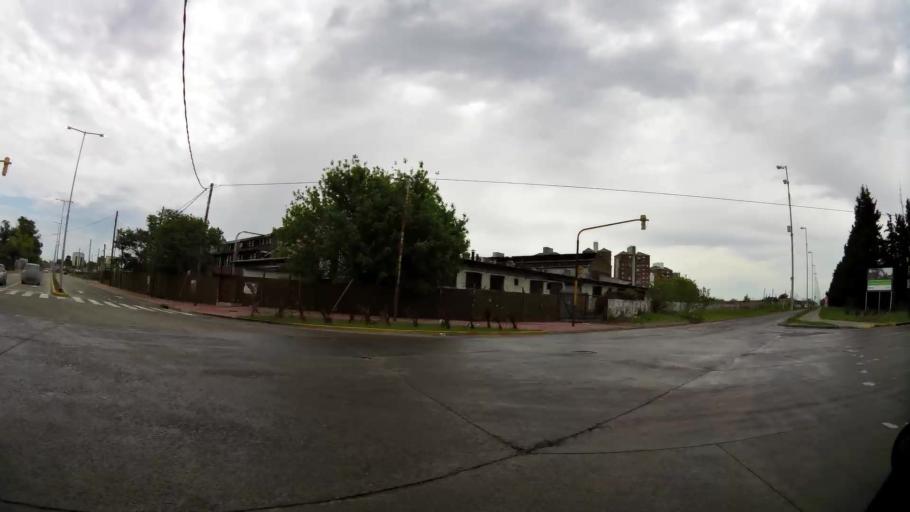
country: AR
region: Buenos Aires
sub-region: Partido de Quilmes
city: Quilmes
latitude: -34.7500
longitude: -58.2225
